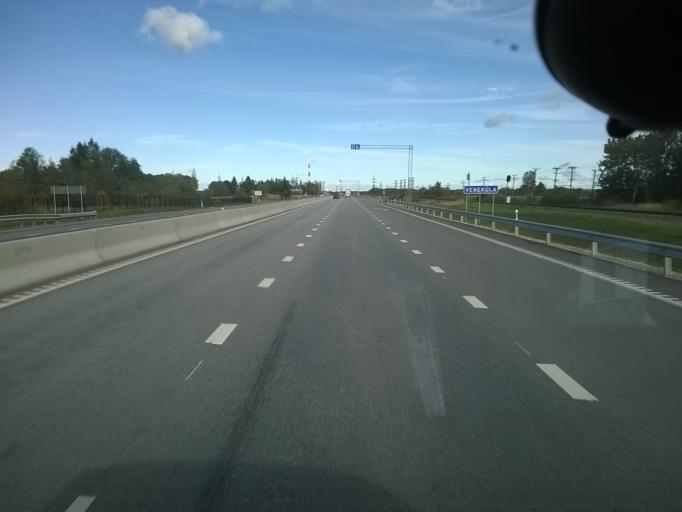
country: EE
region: Harju
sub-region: Joelaehtme vald
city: Loo
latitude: 59.4144
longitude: 24.9191
